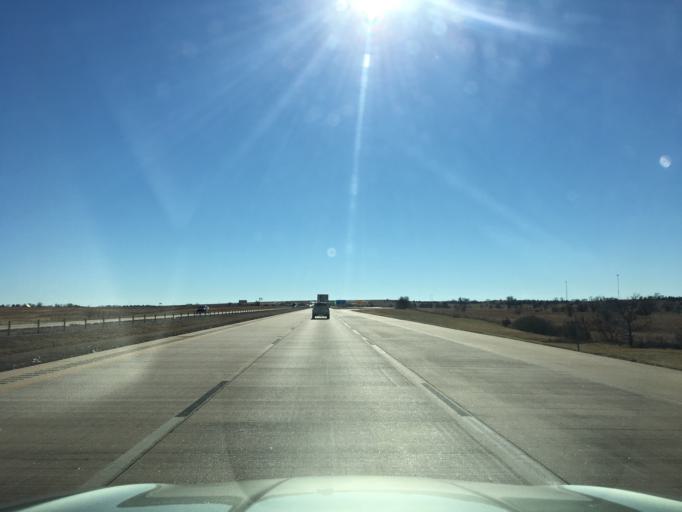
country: US
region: Oklahoma
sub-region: Noble County
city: Perry
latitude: 36.4174
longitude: -97.3272
